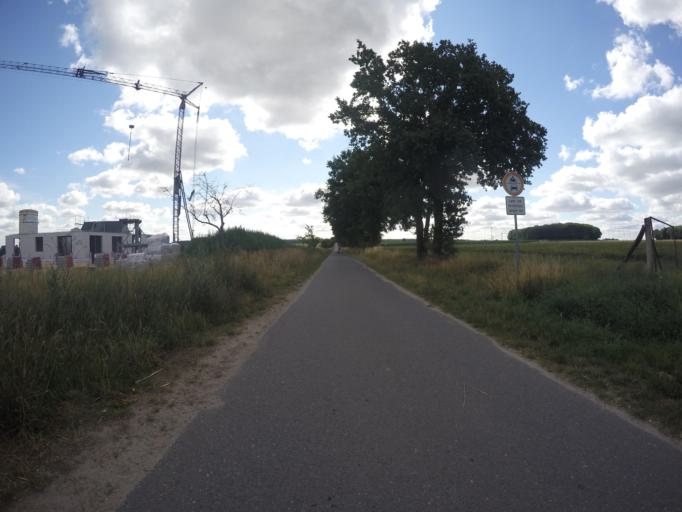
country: DE
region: Lower Saxony
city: Neetze
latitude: 53.2639
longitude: 10.6332
